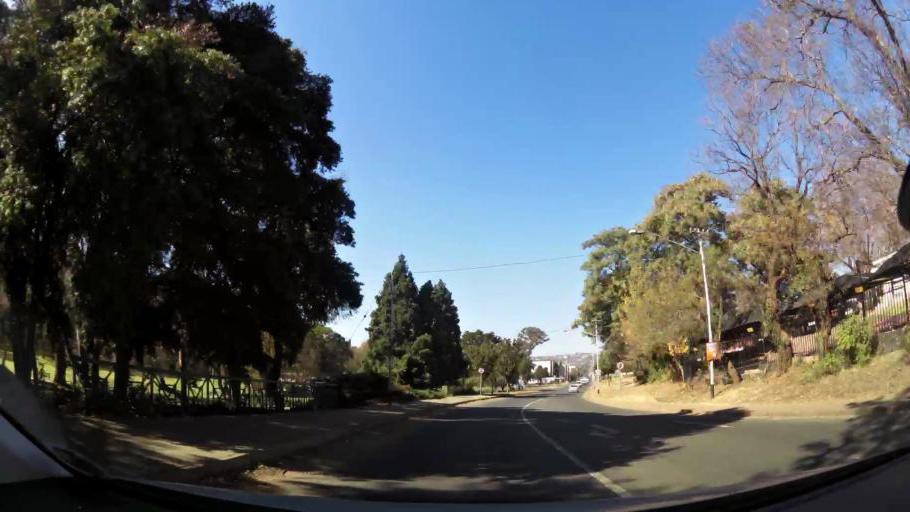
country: ZA
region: Gauteng
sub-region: City of Tshwane Metropolitan Municipality
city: Pretoria
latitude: -25.7627
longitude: 28.2199
